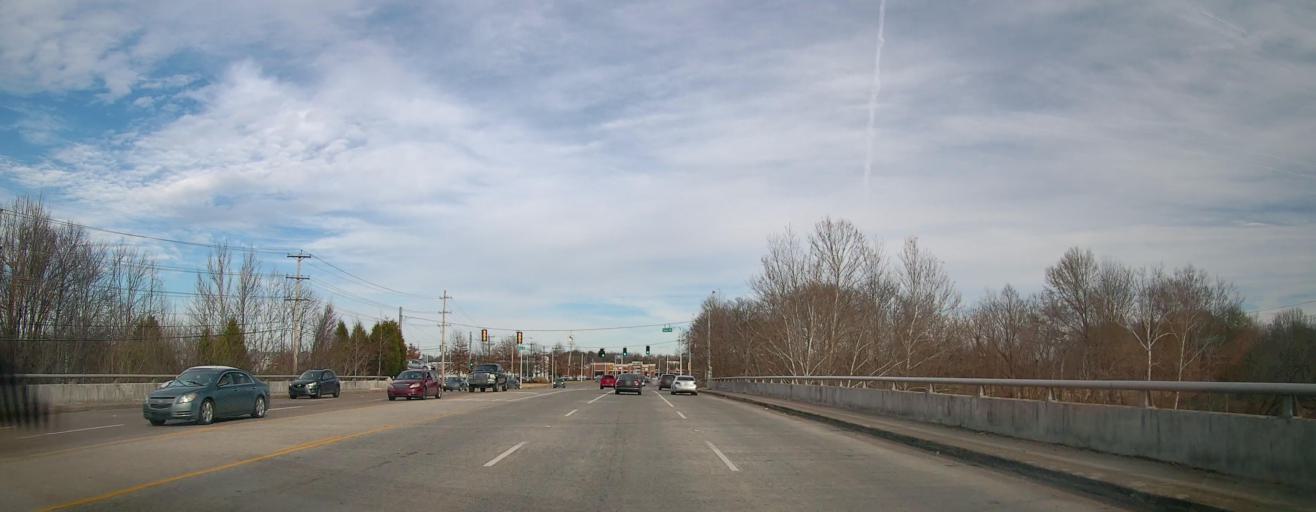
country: US
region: Tennessee
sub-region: Shelby County
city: Germantown
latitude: 35.0495
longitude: -89.8192
